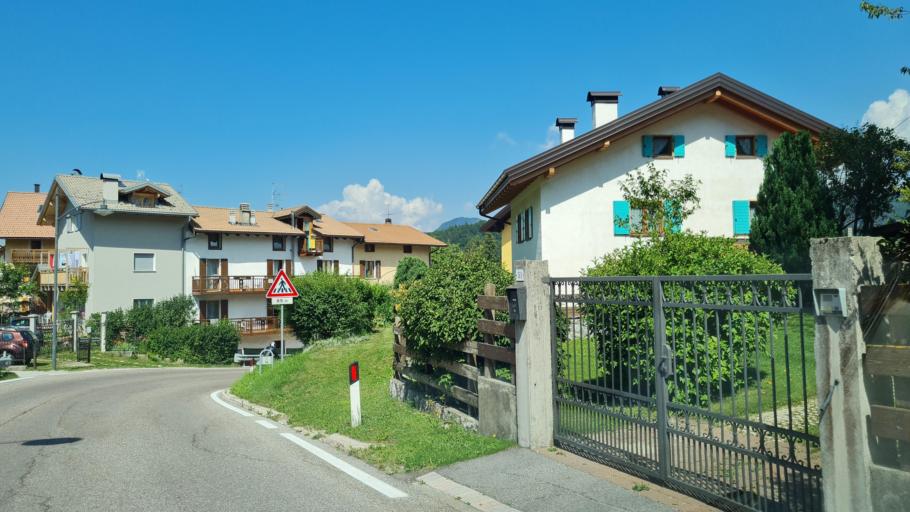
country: IT
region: Trentino-Alto Adige
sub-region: Provincia di Trento
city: Centa San Nicolo
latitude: 45.9327
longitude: 11.2250
